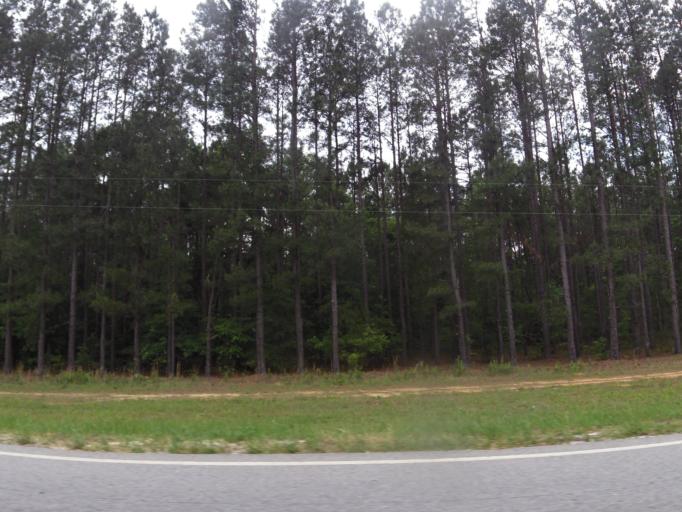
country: US
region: Georgia
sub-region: Emanuel County
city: Twin City
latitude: 32.4757
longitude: -82.2394
